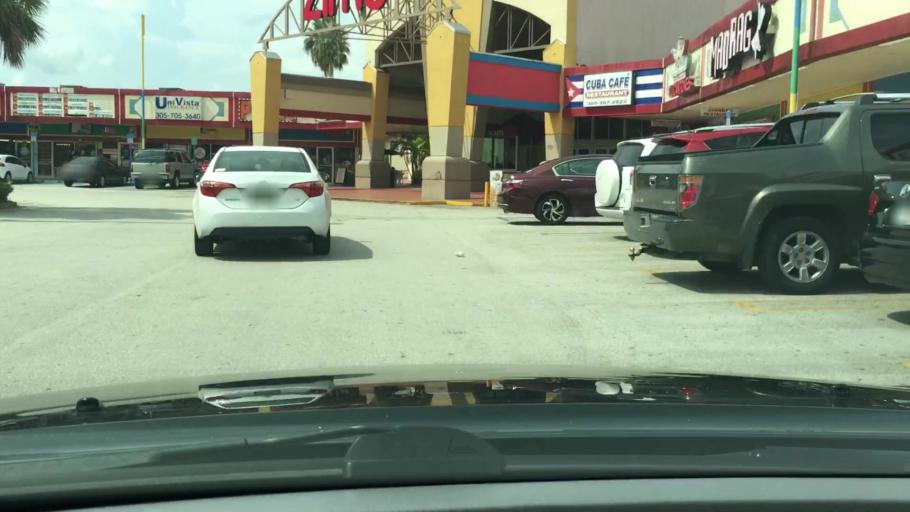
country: US
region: Florida
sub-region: Miami-Dade County
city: Tamiami
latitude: 25.7476
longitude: -80.3888
